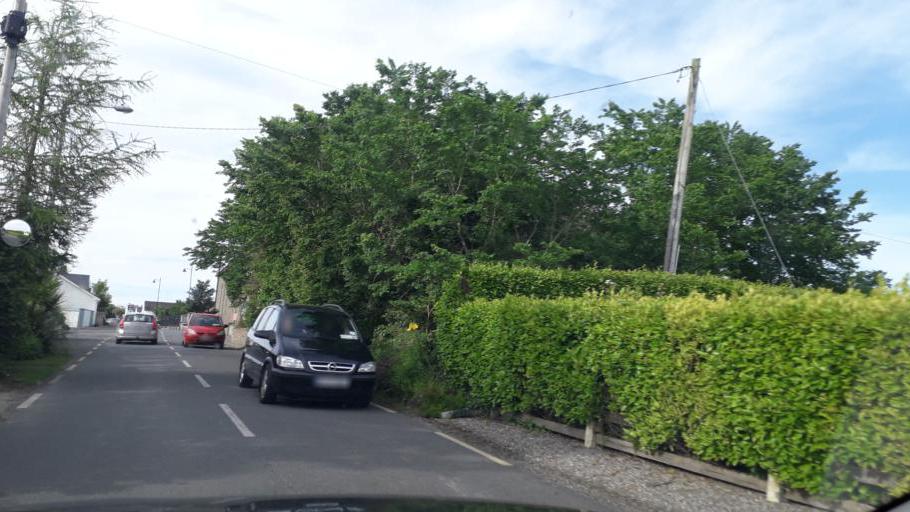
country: IE
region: Leinster
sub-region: Loch Garman
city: Courtown
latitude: 52.5721
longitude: -6.2304
